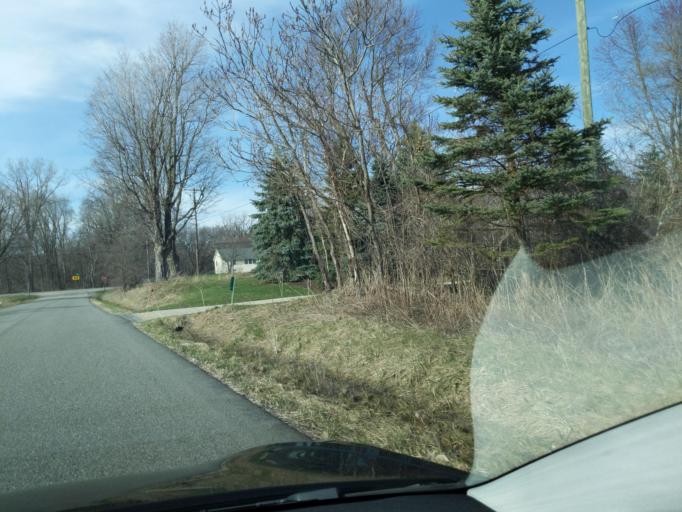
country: US
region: Michigan
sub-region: Ingham County
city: Okemos
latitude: 42.6819
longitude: -84.3834
